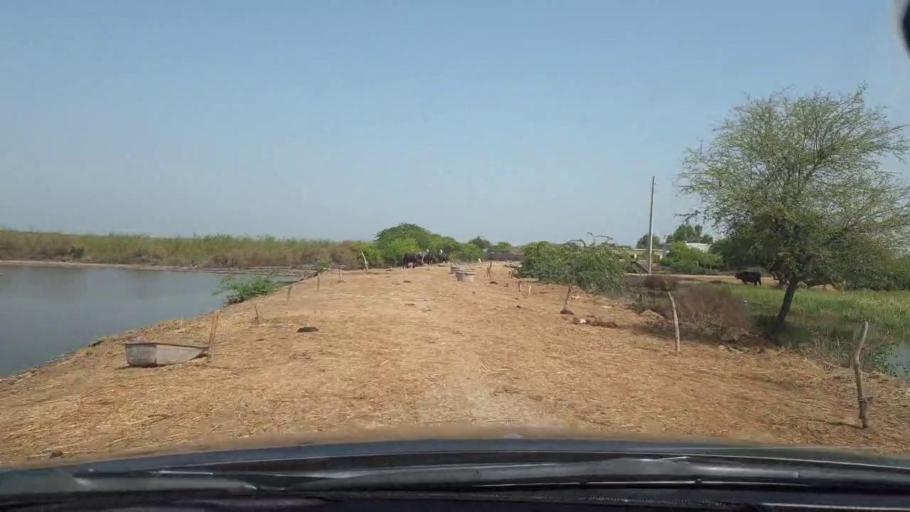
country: PK
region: Sindh
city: Tando Bago
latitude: 24.7887
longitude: 69.0828
